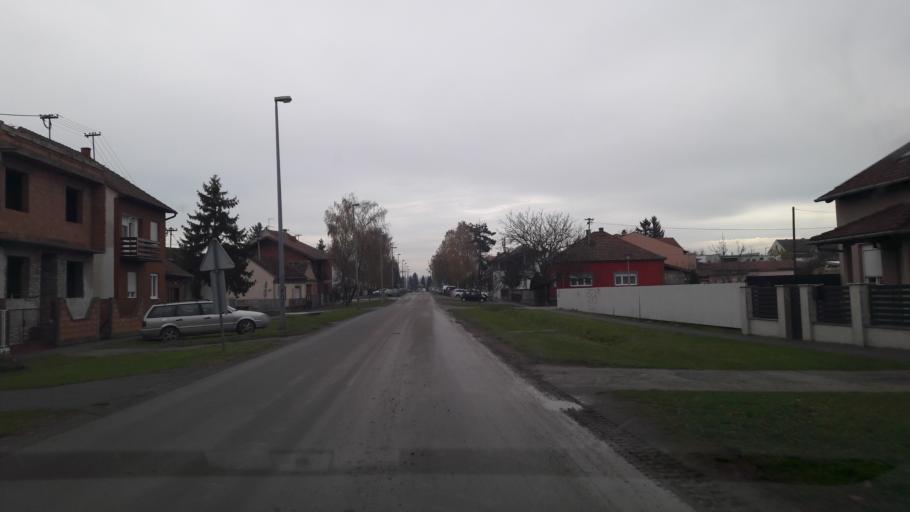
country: HR
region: Osjecko-Baranjska
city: Visnjevac
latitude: 45.5621
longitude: 18.6188
